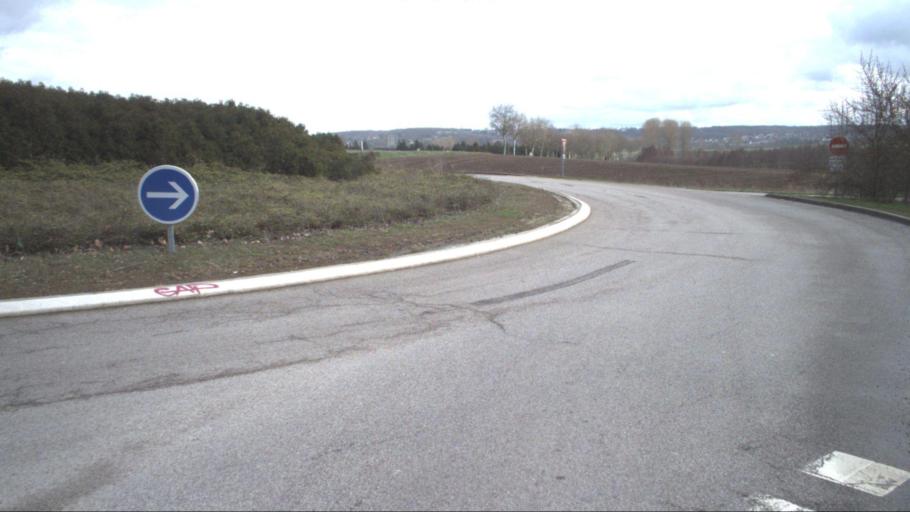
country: FR
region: Ile-de-France
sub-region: Departement des Yvelines
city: Mere
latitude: 48.8008
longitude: 1.8476
